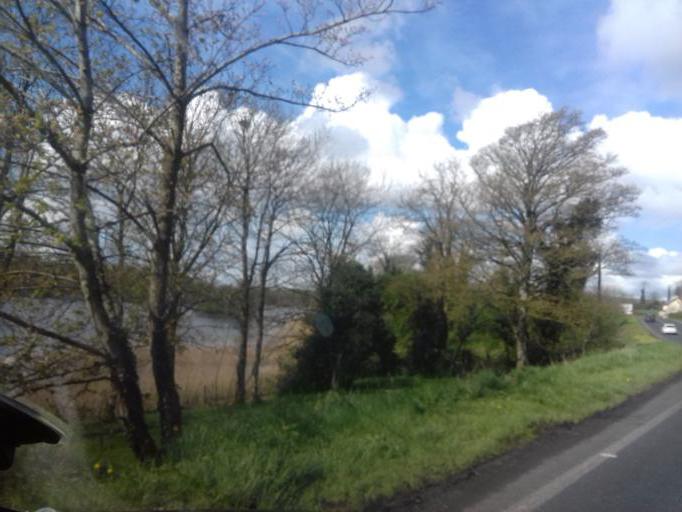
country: IE
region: Ulster
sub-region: An Cabhan
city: Belturbet
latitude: 54.1350
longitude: -7.4921
